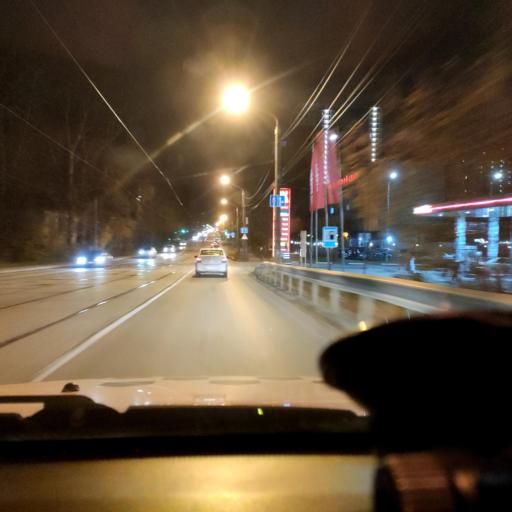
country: RU
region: Perm
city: Perm
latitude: 57.9920
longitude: 56.2181
